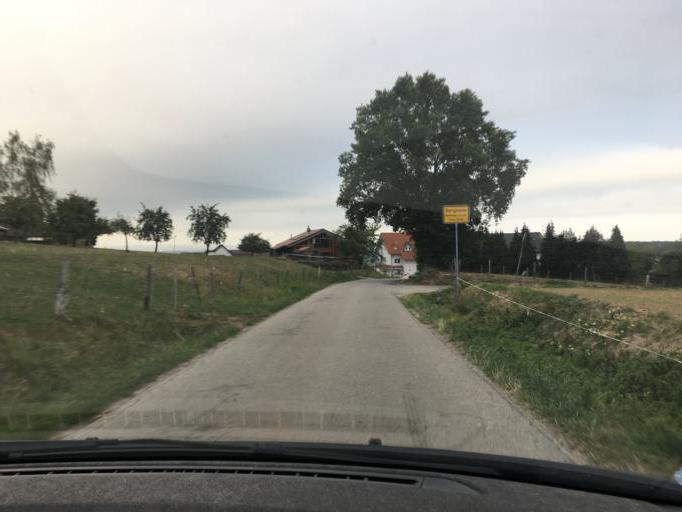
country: DE
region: North Rhine-Westphalia
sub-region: Regierungsbezirk Koln
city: Kreuzau
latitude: 50.7381
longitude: 6.4634
